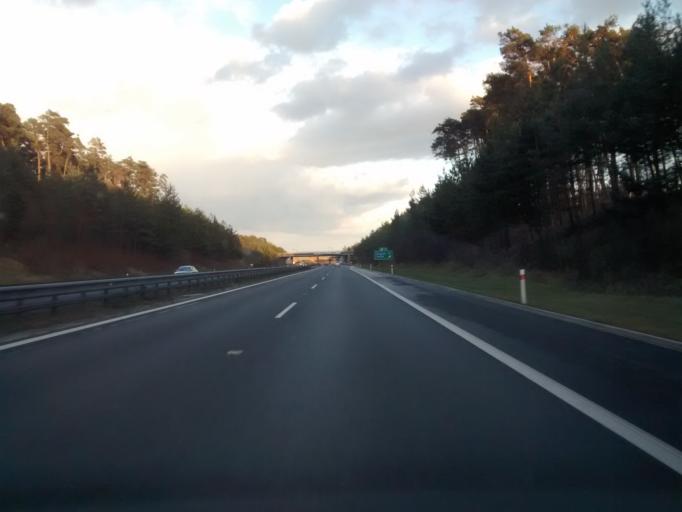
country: CZ
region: Central Bohemia
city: Poricany
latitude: 50.1205
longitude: 14.9371
